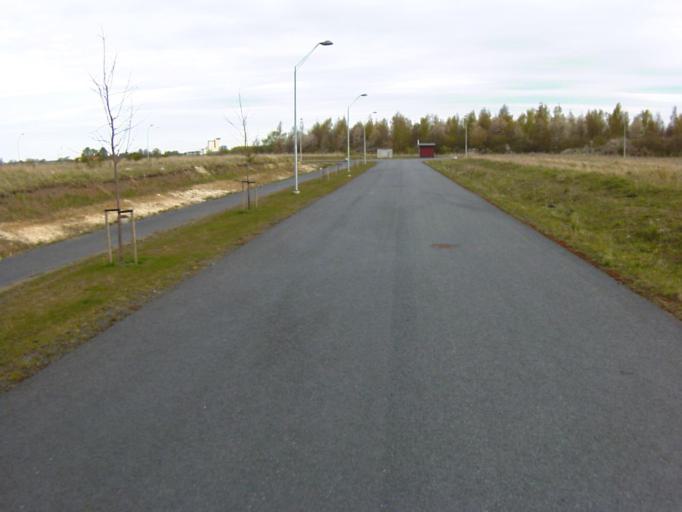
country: SE
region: Skane
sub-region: Kristianstads Kommun
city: Kristianstad
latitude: 56.0248
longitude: 14.1158
